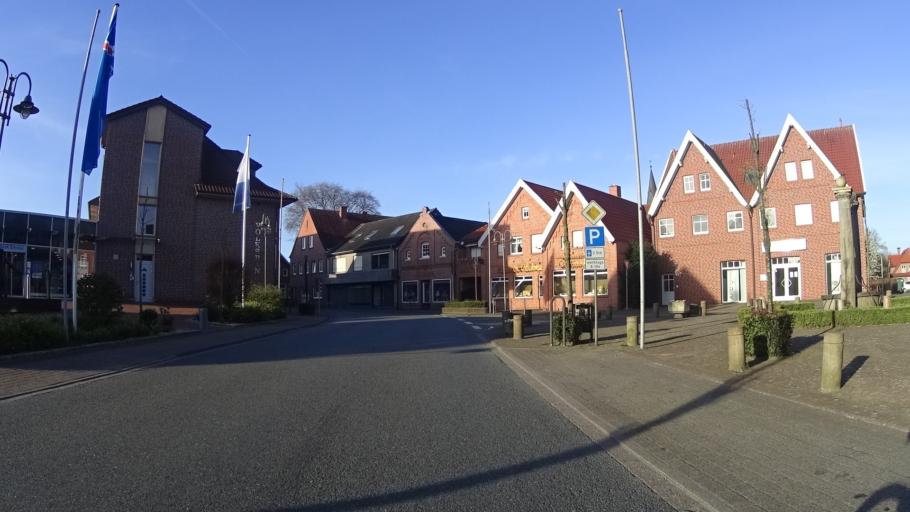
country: DE
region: Lower Saxony
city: Lathen
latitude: 52.8626
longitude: 7.3145
